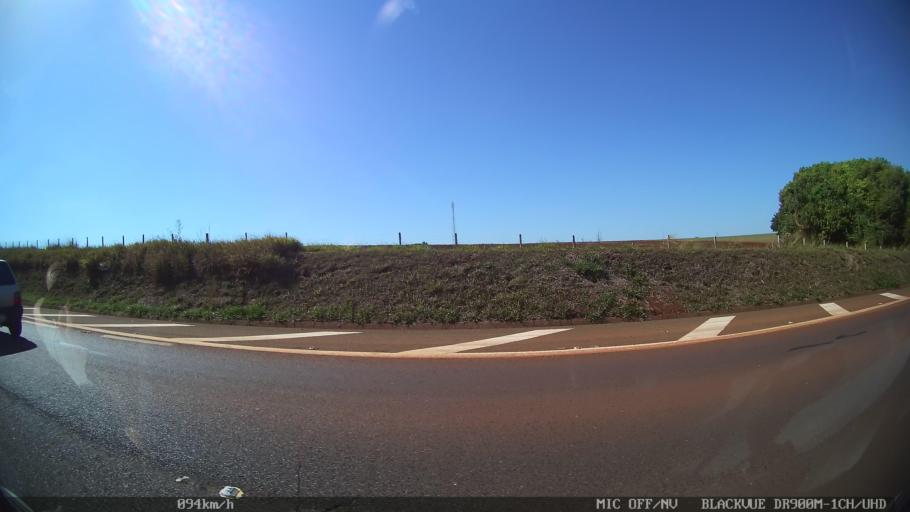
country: BR
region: Sao Paulo
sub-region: Batatais
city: Batatais
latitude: -20.7561
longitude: -47.5315
